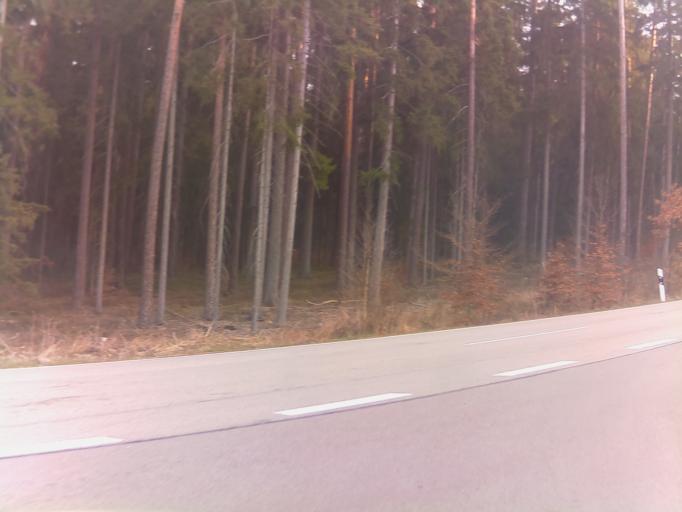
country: DE
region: Bavaria
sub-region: Upper Palatinate
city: Breitenbrunn
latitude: 49.2937
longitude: 12.0098
